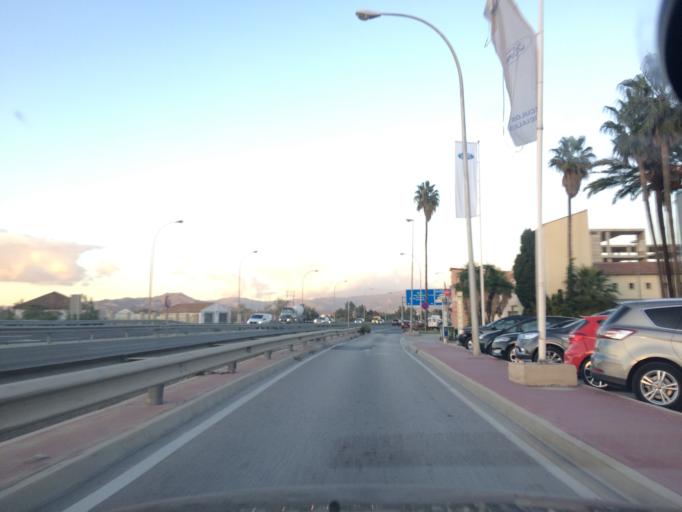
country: ES
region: Andalusia
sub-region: Provincia de Malaga
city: Torremolinos
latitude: 36.6760
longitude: -4.4753
